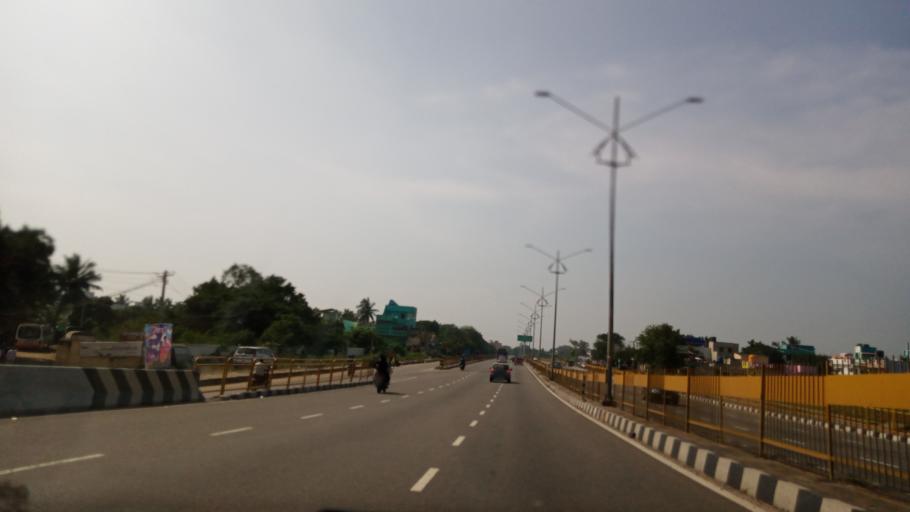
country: IN
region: Tamil Nadu
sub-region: Vellore
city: Vellore
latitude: 12.9219
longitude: 79.1073
